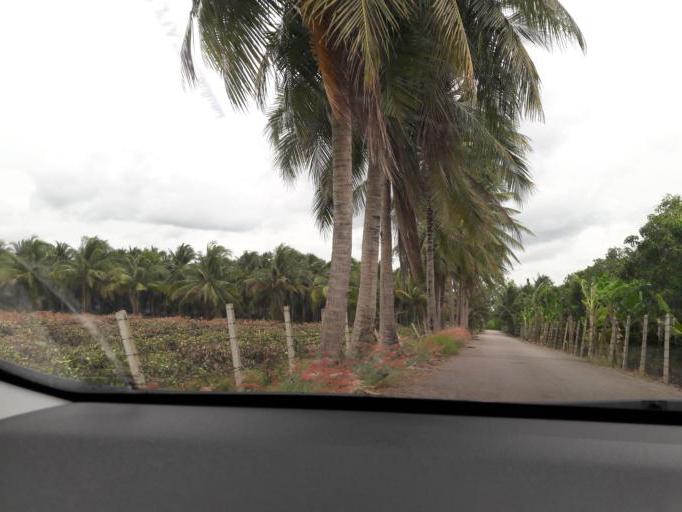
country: TH
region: Ratchaburi
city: Damnoen Saduak
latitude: 13.5567
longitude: 100.0300
